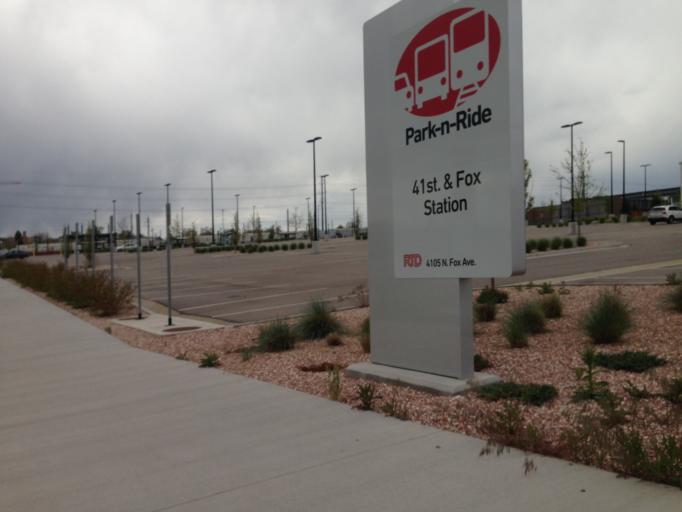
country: US
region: Colorado
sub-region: Denver County
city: Denver
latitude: 39.7730
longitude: -104.9950
